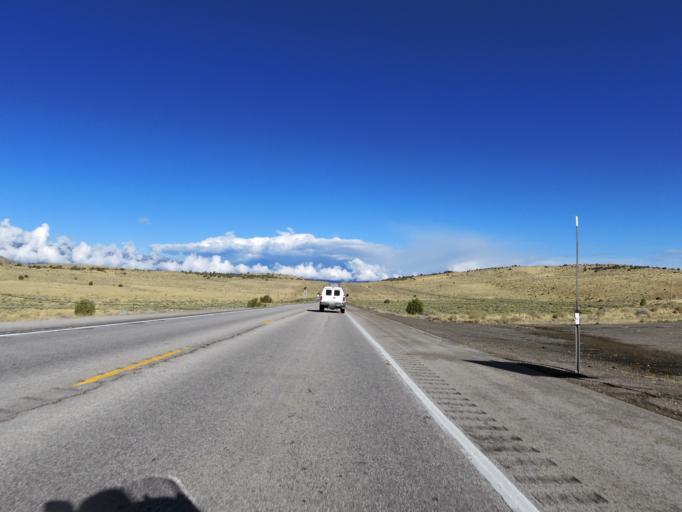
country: US
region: Nevada
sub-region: Douglas County
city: Gardnerville Ranchos
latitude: 38.8564
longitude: -119.6642
